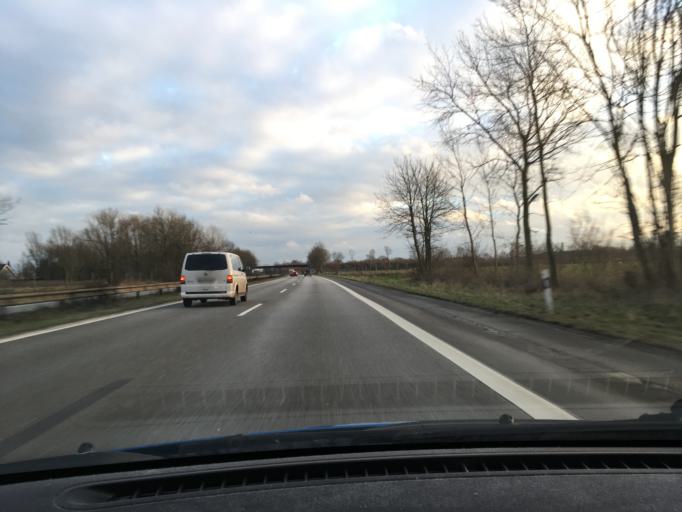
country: DE
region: Schleswig-Holstein
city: Seeth-Ekholt
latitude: 53.7308
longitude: 9.7243
